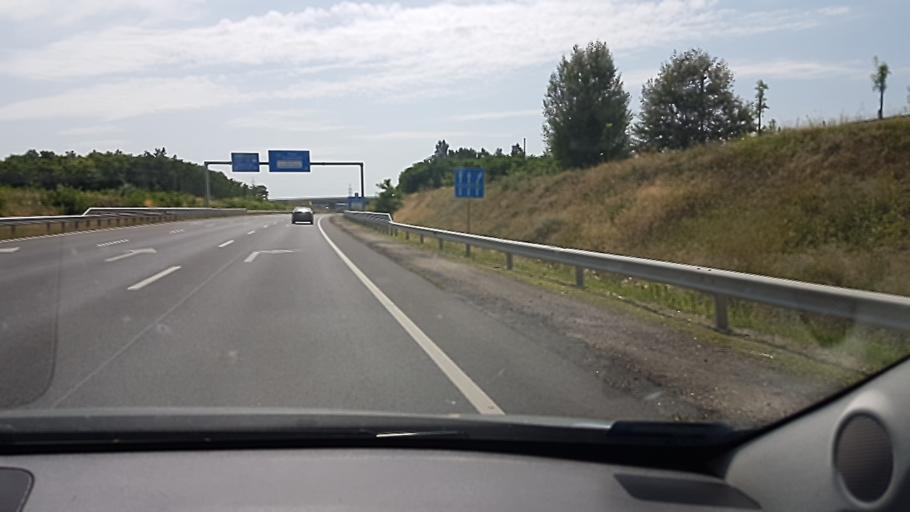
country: HU
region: Budapest
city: Budapest XXIII. keruelet
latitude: 47.3716
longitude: 19.1270
